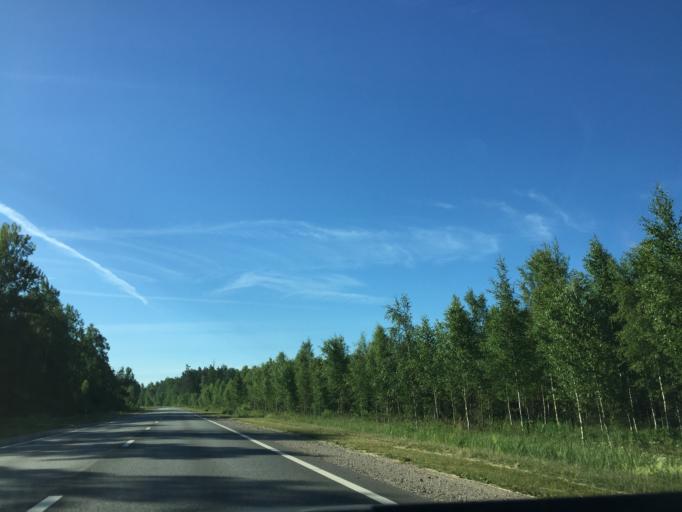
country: LV
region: Ventspils
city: Ventspils
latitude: 57.3829
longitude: 21.7102
